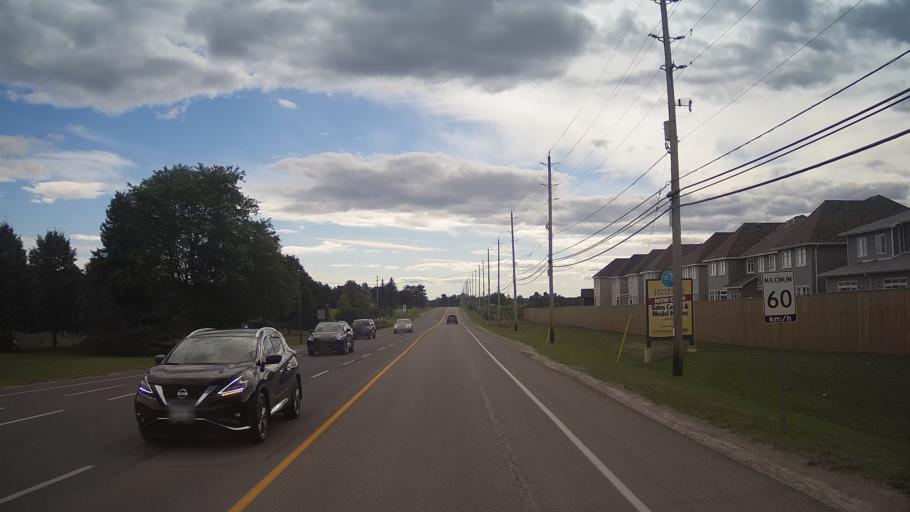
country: CA
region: Ontario
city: Kingston
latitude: 44.2682
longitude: -76.4523
